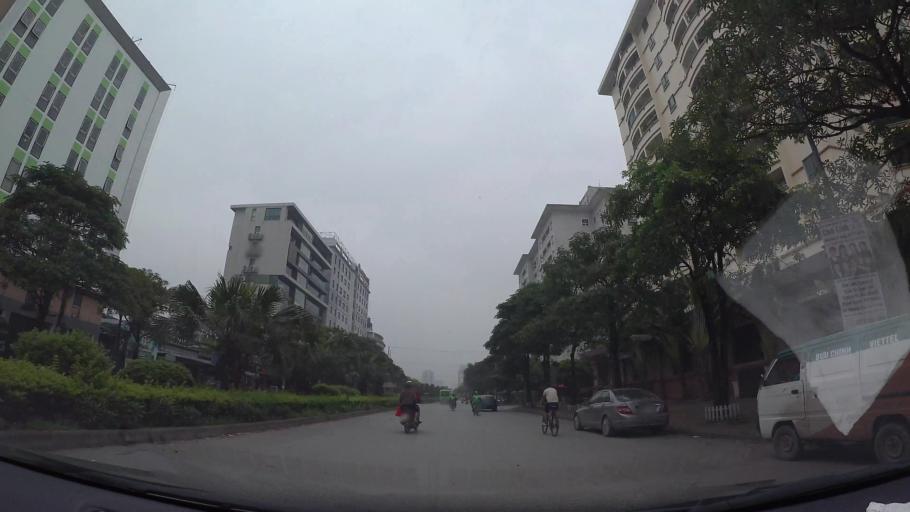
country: VN
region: Ha Noi
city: Hai BaTrung
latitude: 20.9838
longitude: 105.8663
